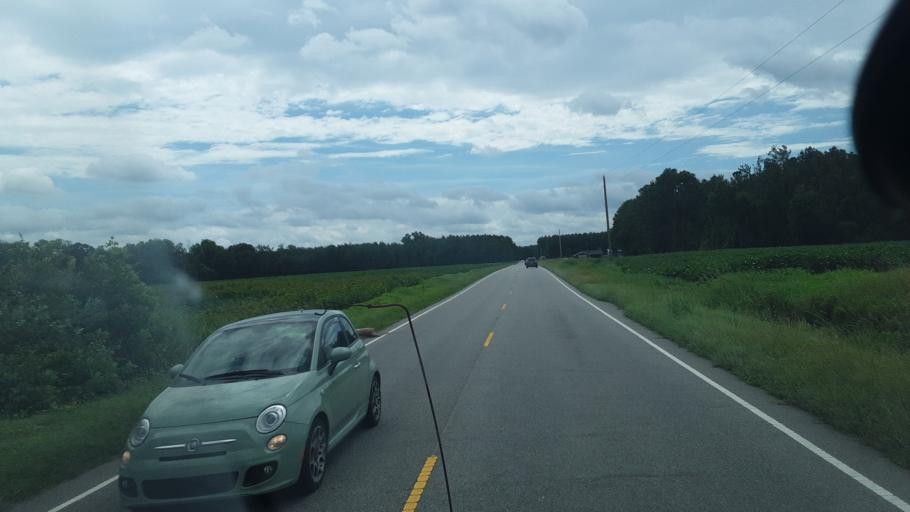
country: US
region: North Carolina
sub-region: Robeson County
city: Rowland
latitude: 34.6300
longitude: -79.3388
